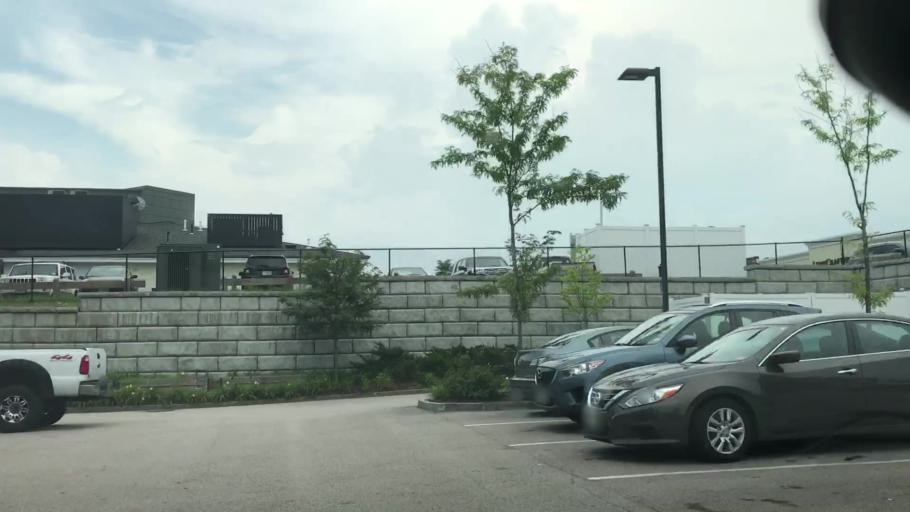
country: US
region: Massachusetts
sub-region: Middlesex County
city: Tyngsboro
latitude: 42.7129
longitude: -71.4432
